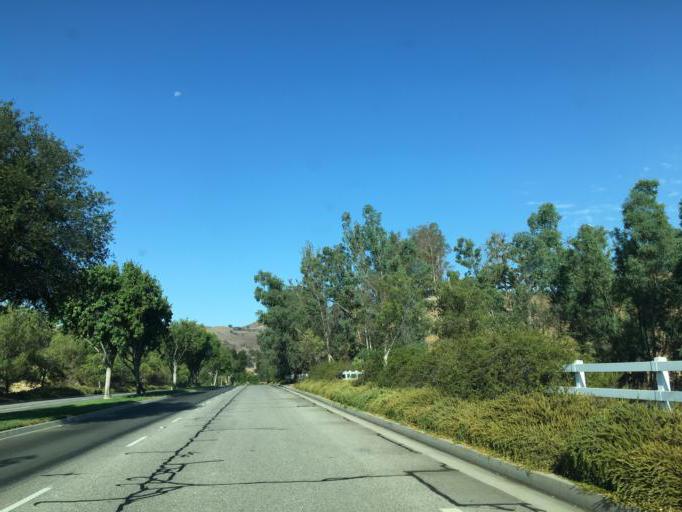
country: US
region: California
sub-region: Los Angeles County
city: Hidden Hills
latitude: 34.1523
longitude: -118.6860
